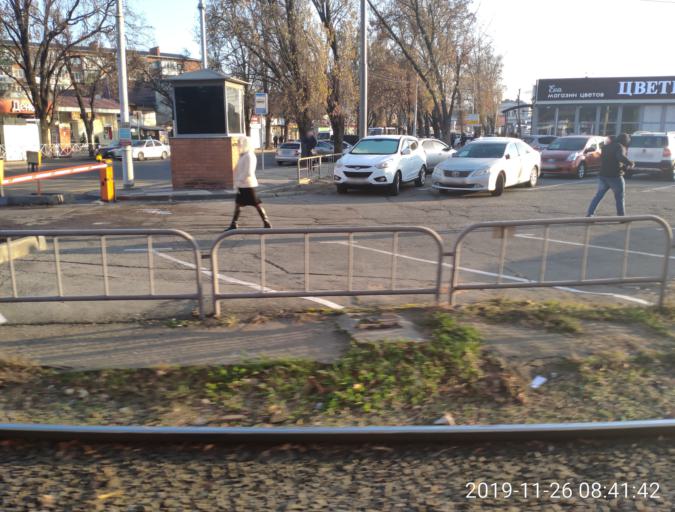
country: RU
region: Krasnodarskiy
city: Krasnodar
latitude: 45.0534
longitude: 38.9836
